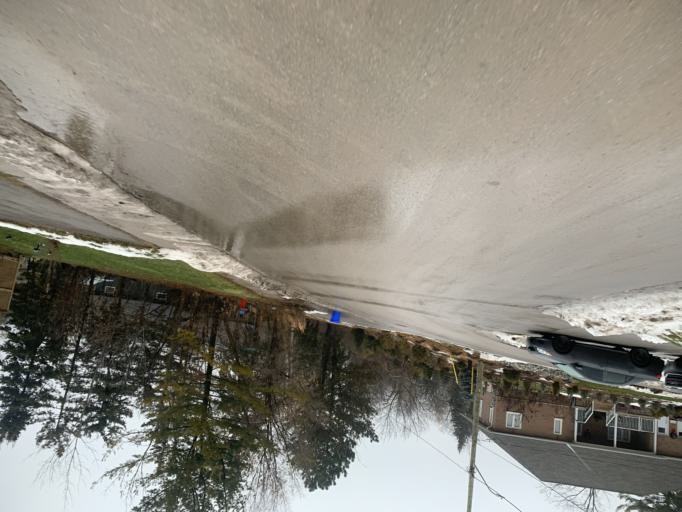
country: CA
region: Ontario
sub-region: Halton
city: Milton
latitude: 43.6556
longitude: -79.9309
